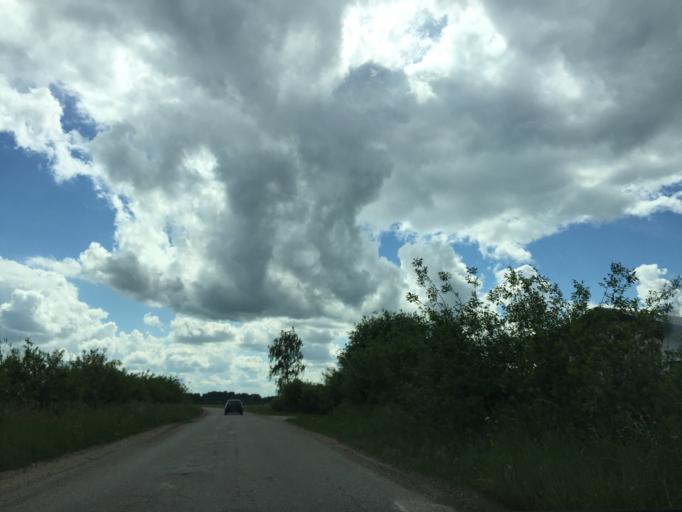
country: LV
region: Dobeles Rajons
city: Dobele
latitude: 56.6965
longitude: 23.4552
